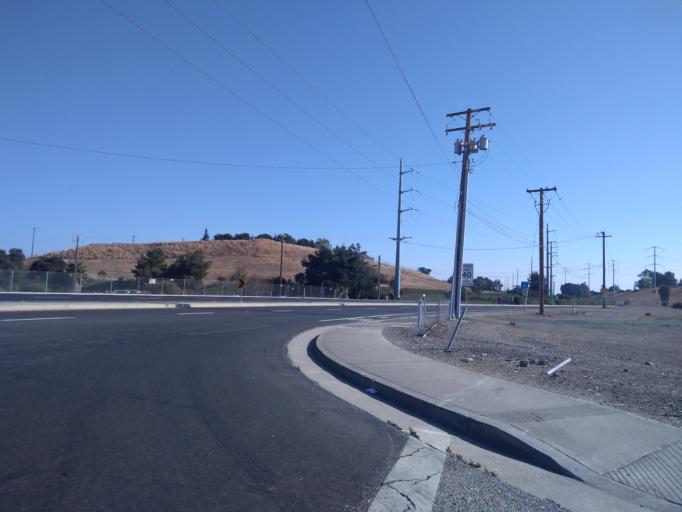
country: US
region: California
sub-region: Santa Clara County
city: Santa Clara
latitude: 37.4167
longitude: -121.9728
